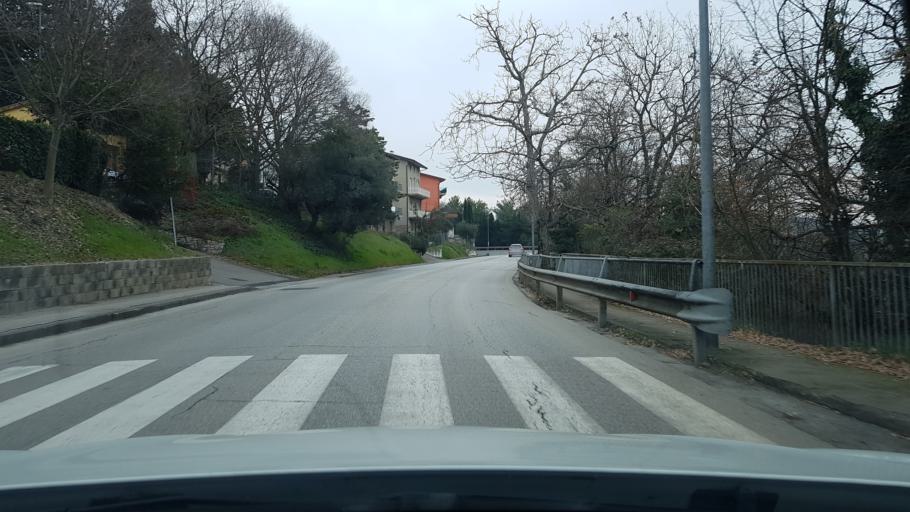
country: IT
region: Umbria
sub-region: Provincia di Perugia
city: Lacugnano
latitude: 43.1023
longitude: 12.3491
